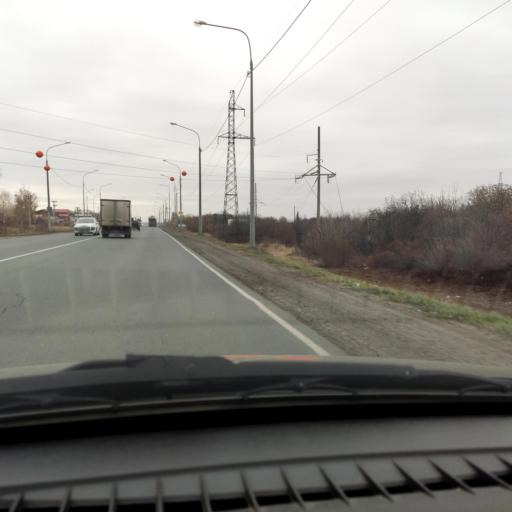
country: RU
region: Samara
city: Zhigulevsk
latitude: 53.3825
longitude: 49.4558
